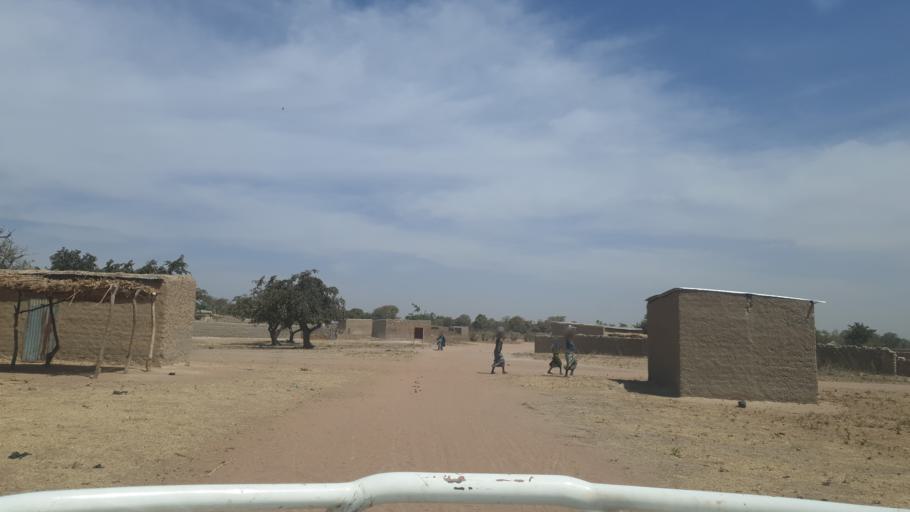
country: ML
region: Sikasso
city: Yorosso
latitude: 12.2927
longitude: -4.6466
